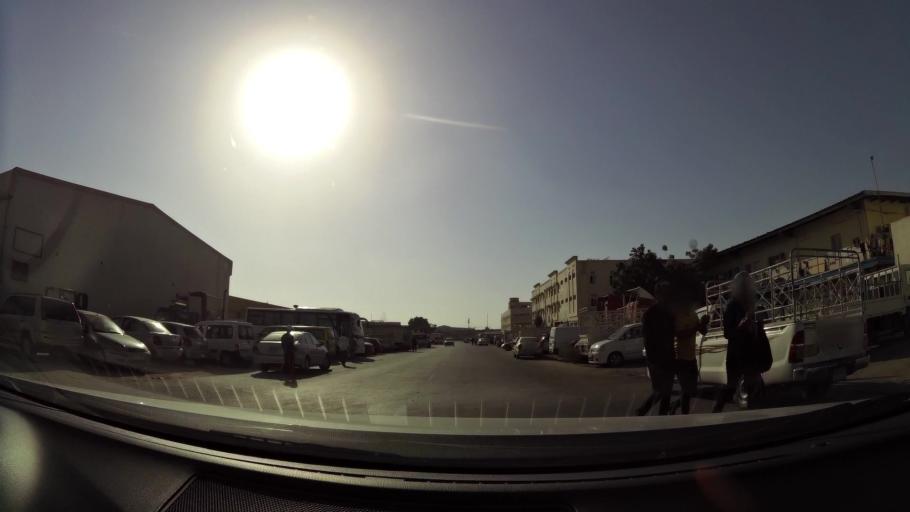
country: AE
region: Dubai
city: Dubai
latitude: 25.1218
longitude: 55.2288
